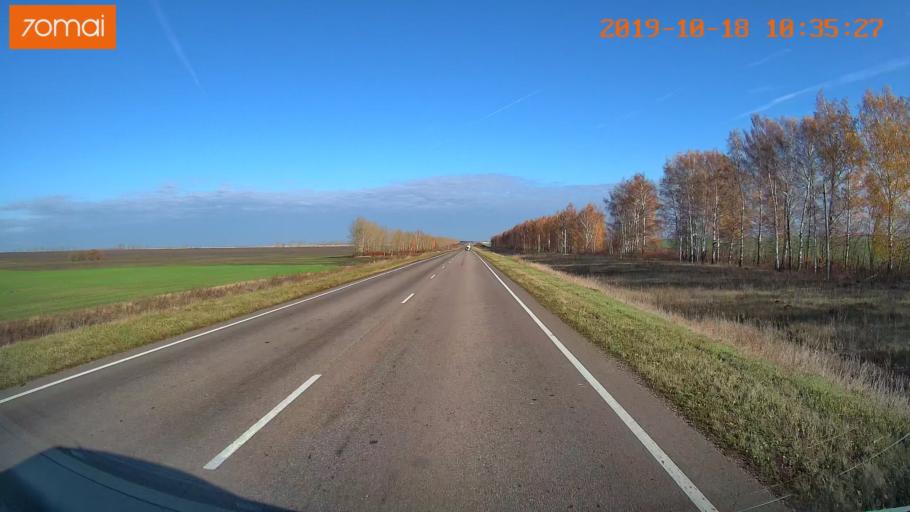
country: RU
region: Tula
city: Kurkino
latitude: 53.5332
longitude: 38.6199
